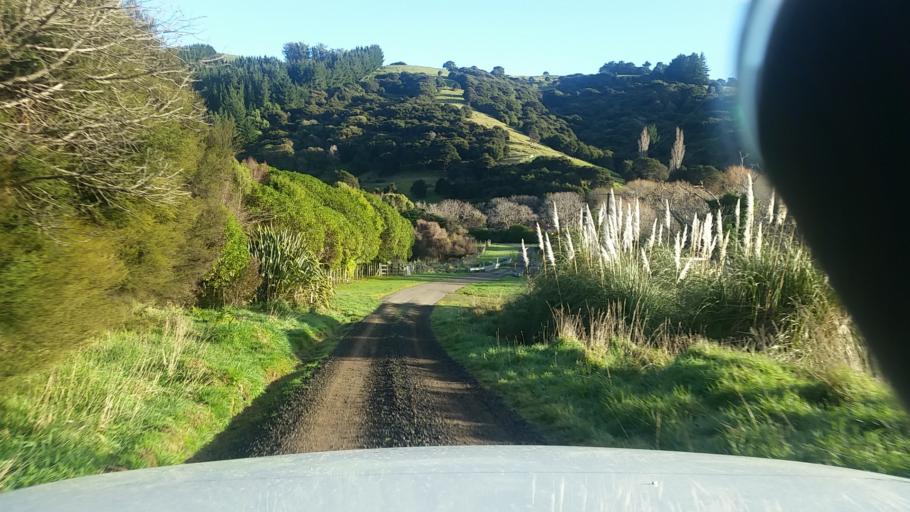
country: NZ
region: Canterbury
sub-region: Christchurch City
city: Christchurch
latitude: -43.7589
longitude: 172.9709
